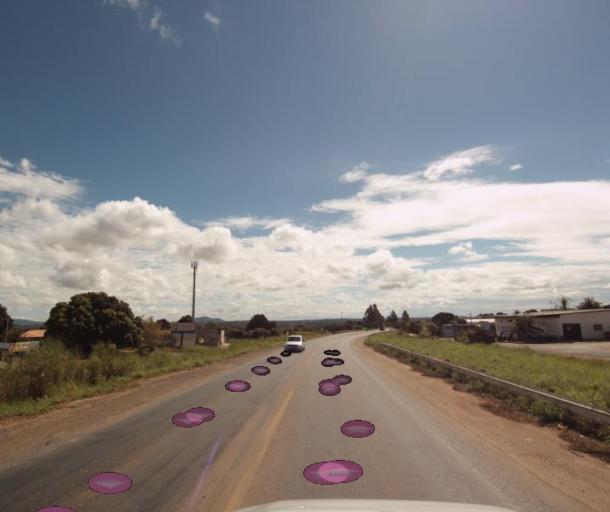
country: BR
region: Goias
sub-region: Uruacu
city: Uruacu
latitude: -14.5242
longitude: -49.1587
